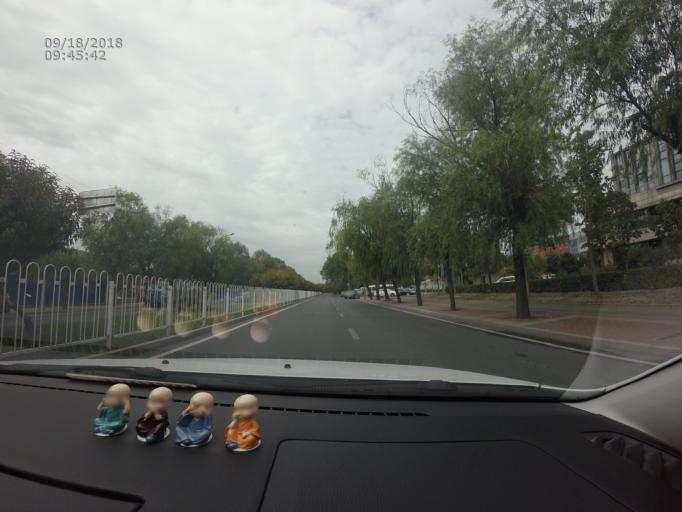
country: CN
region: Beijing
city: Xibeiwang
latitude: 40.0697
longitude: 116.2376
